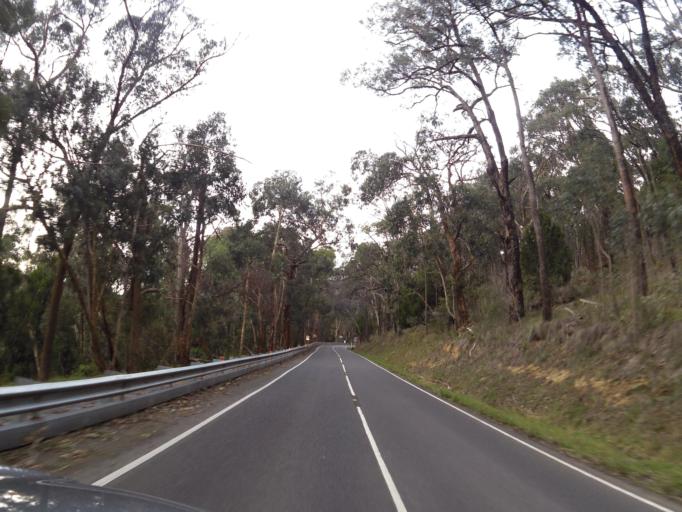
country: AU
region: Victoria
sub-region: Yarra Ranges
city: Ferny Creek
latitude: -37.8669
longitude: 145.3250
